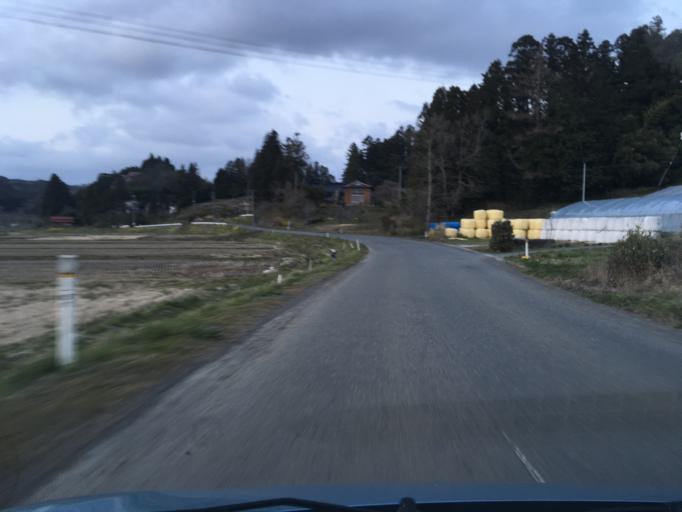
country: JP
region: Iwate
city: Ichinoseki
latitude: 38.7861
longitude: 141.2408
